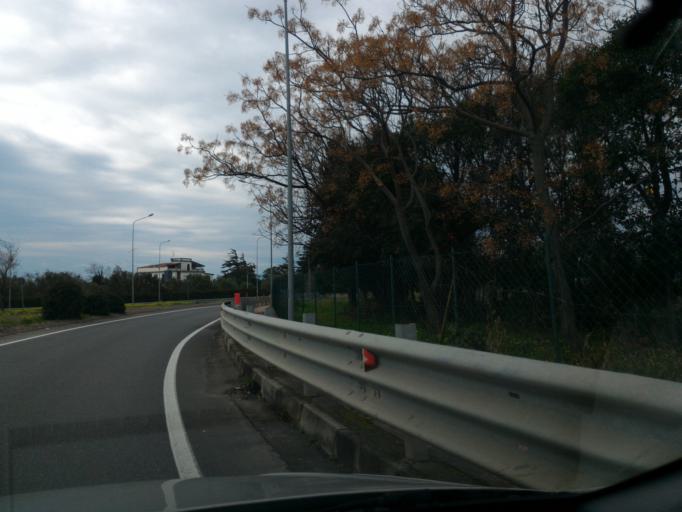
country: IT
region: Calabria
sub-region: Provincia di Catanzaro
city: Barone
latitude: 38.8429
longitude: 16.6490
